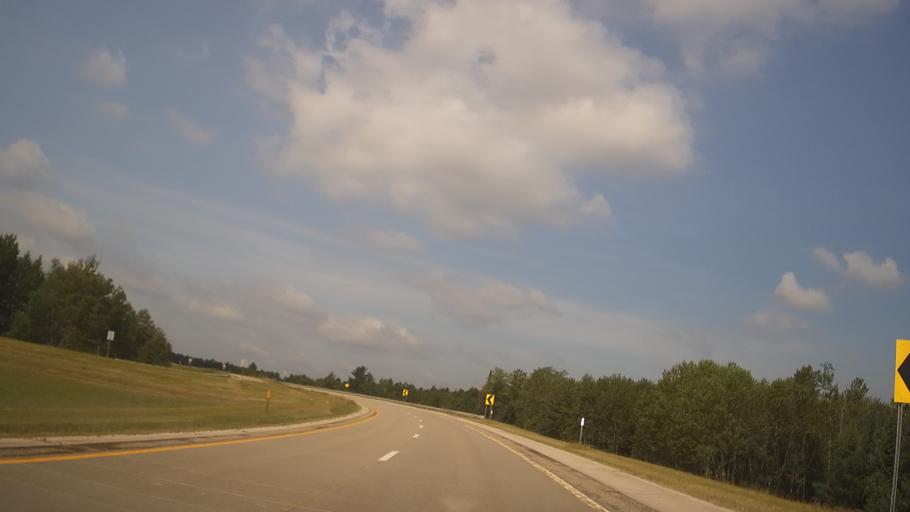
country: US
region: Michigan
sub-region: Roscommon County
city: Saint Helen
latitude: 44.3157
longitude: -84.4982
